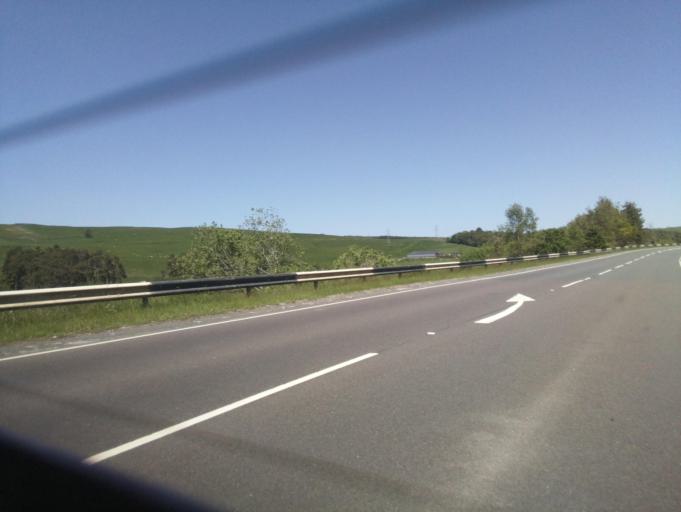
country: GB
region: Scotland
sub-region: The Scottish Borders
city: Hawick
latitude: 55.3517
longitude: -2.9167
